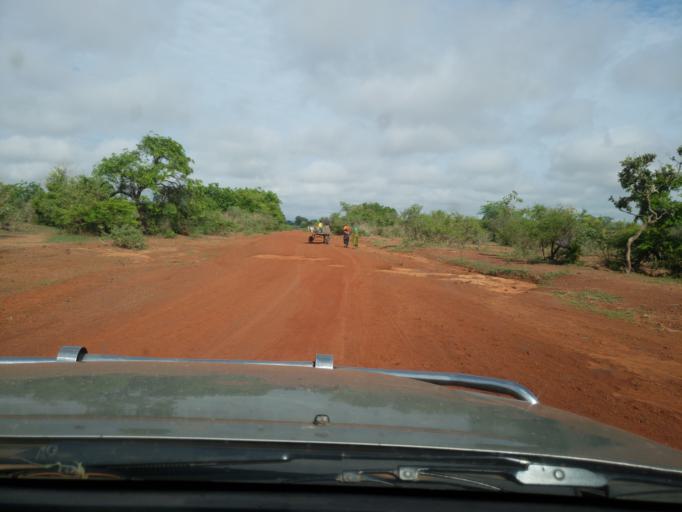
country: ML
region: Sikasso
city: Koutiala
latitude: 12.3933
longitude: -5.9802
